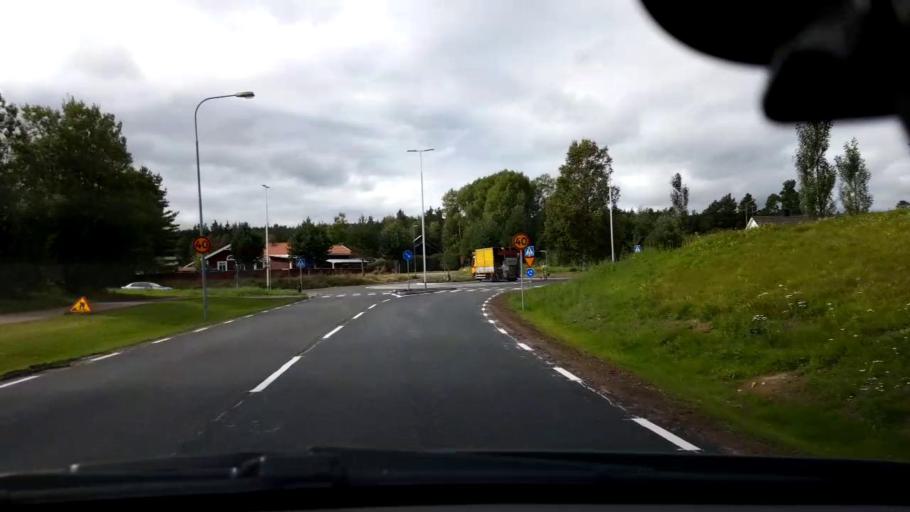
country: SE
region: Dalarna
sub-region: Borlange Kommun
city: Borlaenge
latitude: 60.4870
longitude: 15.3930
